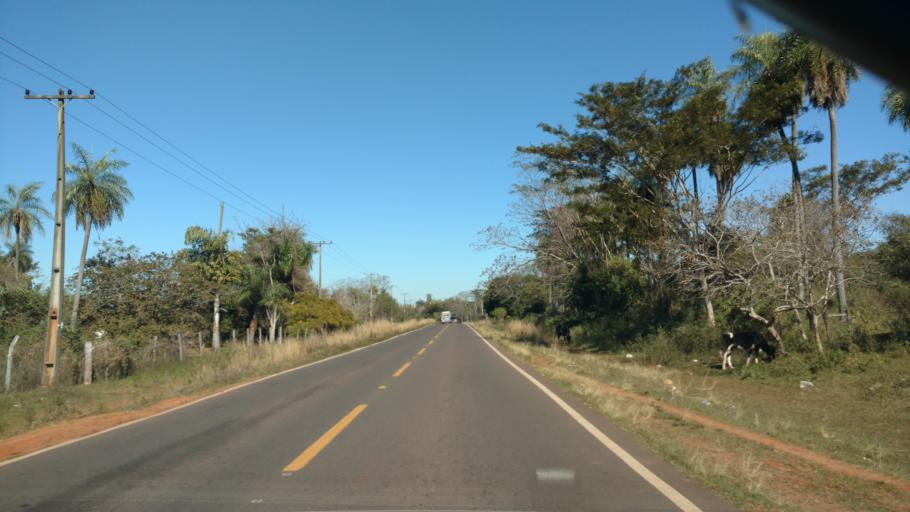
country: PY
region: Paraguari
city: Pirayu
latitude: -25.5224
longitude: -57.2668
